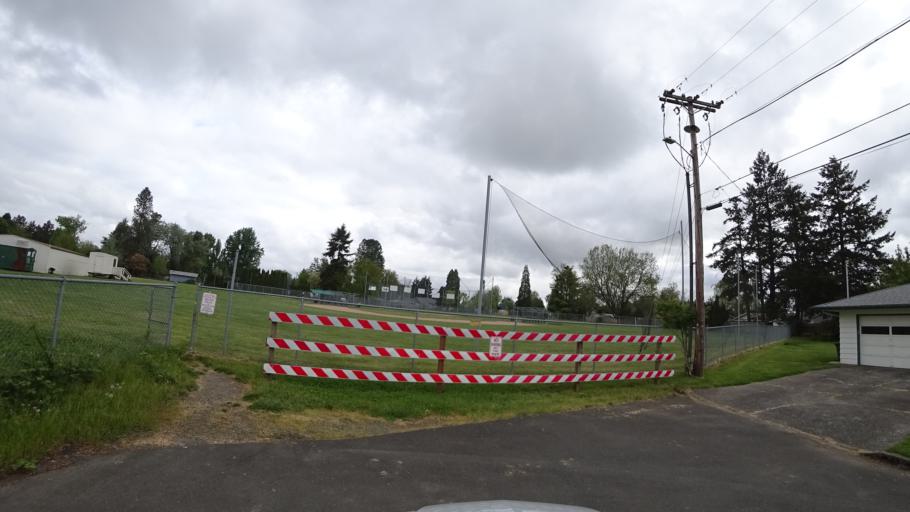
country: US
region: Oregon
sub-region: Washington County
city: Hillsboro
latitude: 45.5331
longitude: -122.9705
